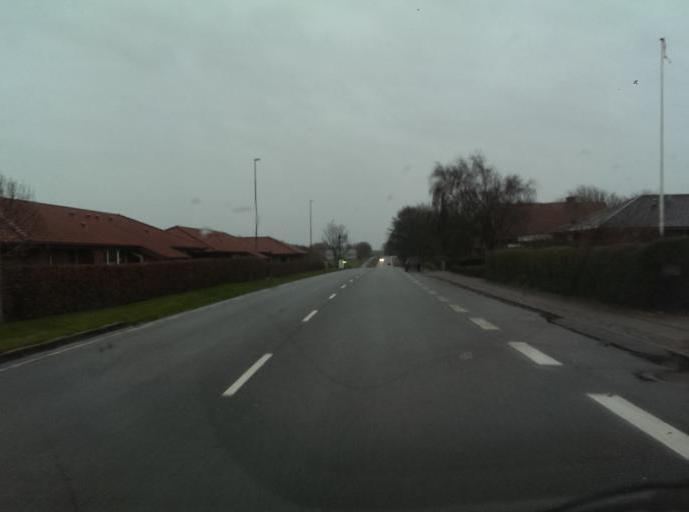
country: DK
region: South Denmark
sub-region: Esbjerg Kommune
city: Tjaereborg
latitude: 55.4993
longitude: 8.5323
